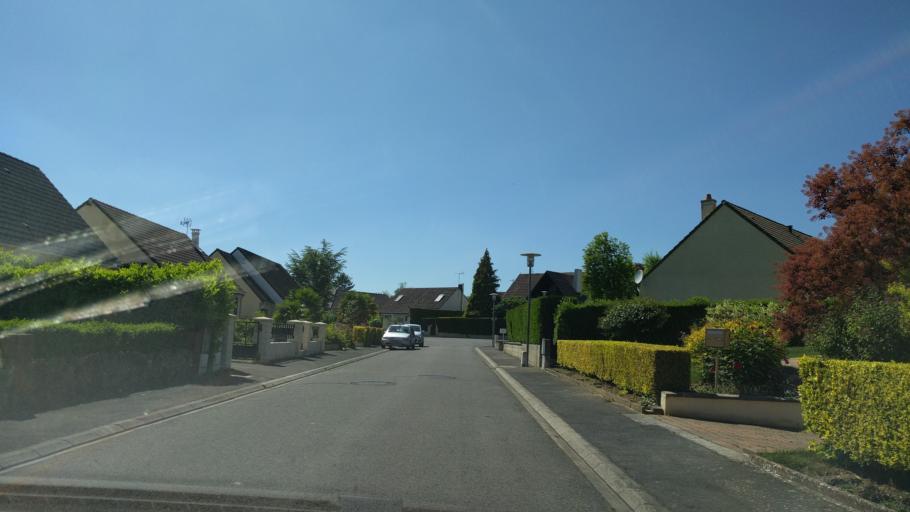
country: FR
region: Picardie
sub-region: Departement de la Somme
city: Peronne
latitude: 49.9419
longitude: 2.9386
